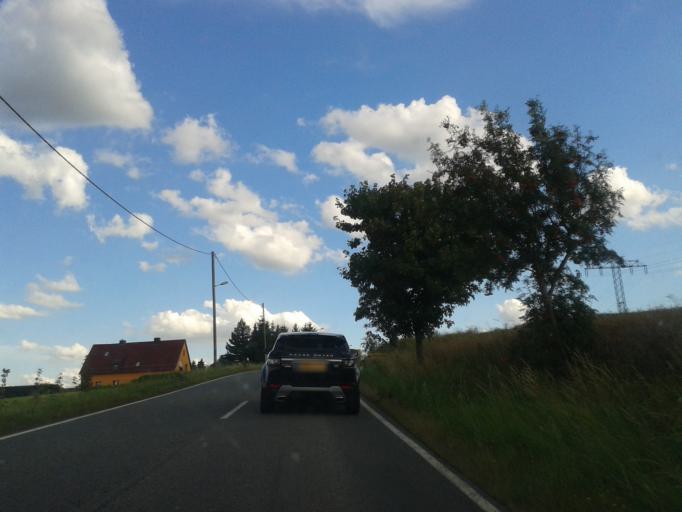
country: DE
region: Saxony
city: Radeberg
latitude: 51.0597
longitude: 13.9354
